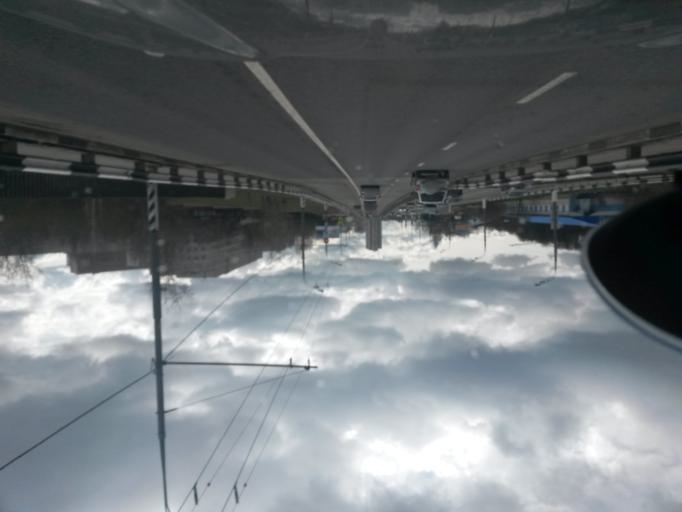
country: RU
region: Moscow
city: Yasenevo
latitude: 55.6285
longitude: 37.5403
